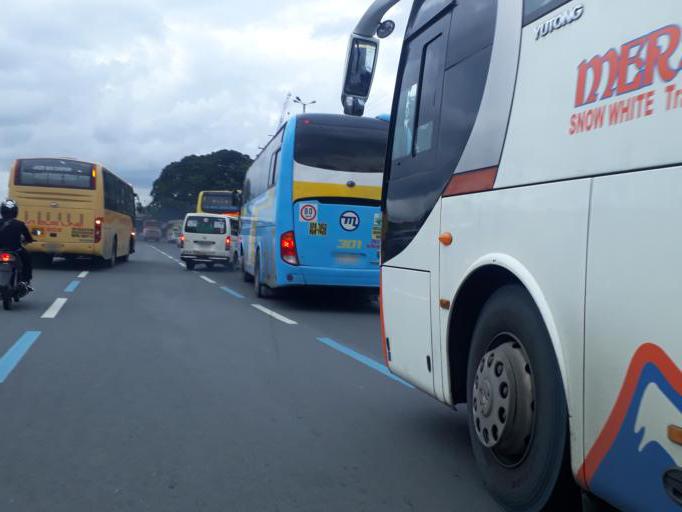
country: PH
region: Calabarzon
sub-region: Province of Rizal
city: San Mateo
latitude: 14.6791
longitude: 121.0840
